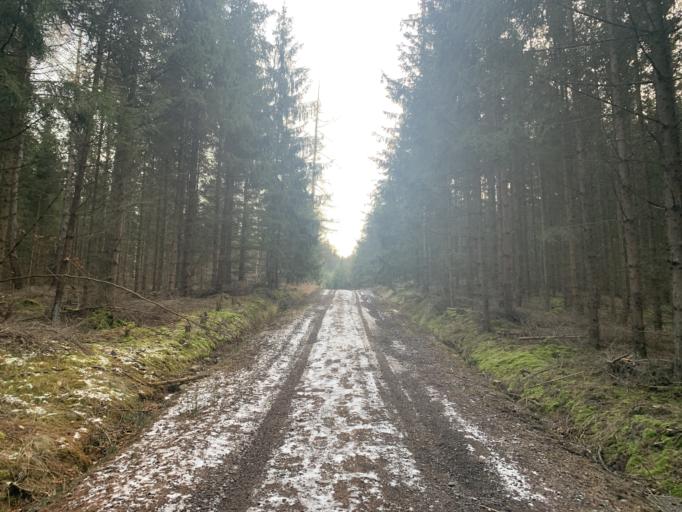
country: CZ
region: Plzensky
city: Zbiroh
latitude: 49.8230
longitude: 13.7975
